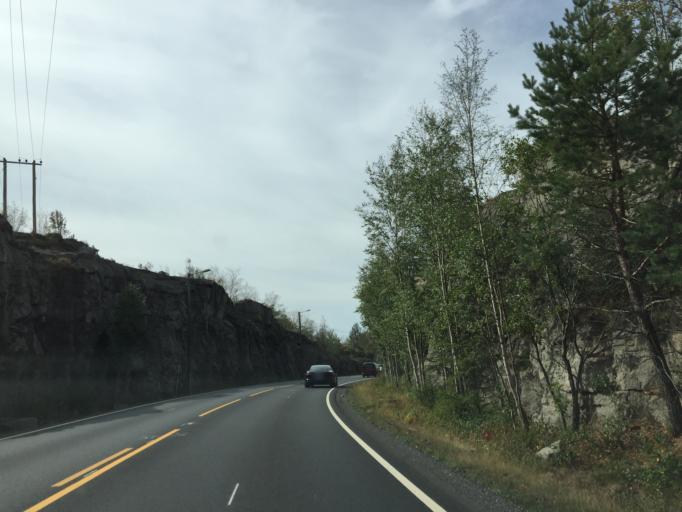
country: NO
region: Ostfold
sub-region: Fredrikstad
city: Fredrikstad
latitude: 59.1365
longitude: 10.9426
